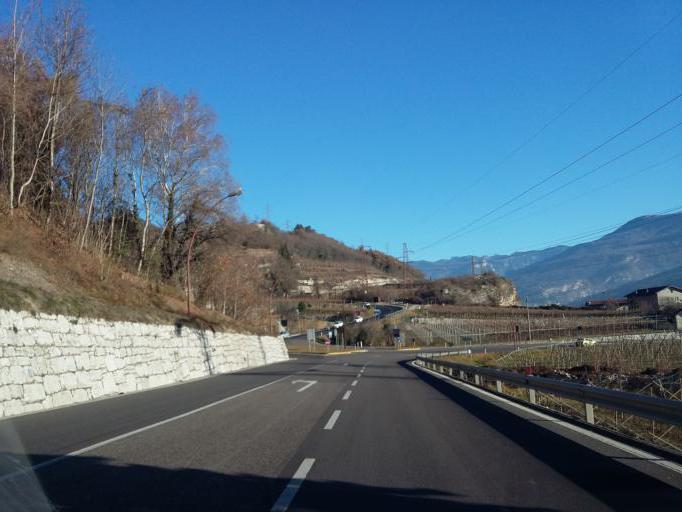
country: IT
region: Trentino-Alto Adige
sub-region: Provincia di Trento
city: Mori
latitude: 45.8630
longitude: 10.9947
